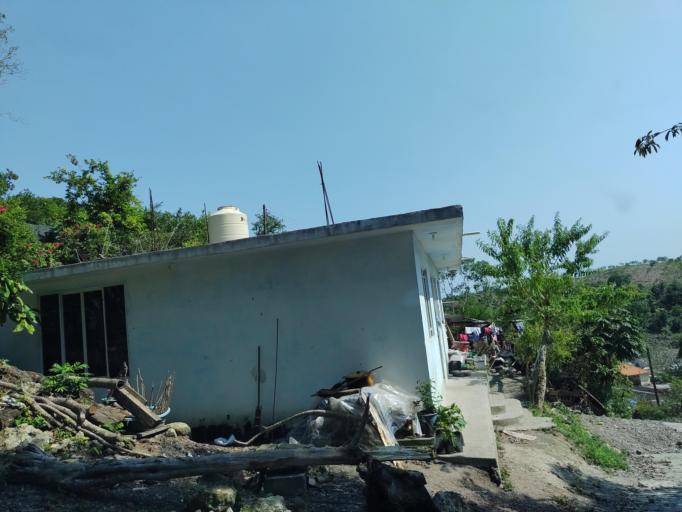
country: MX
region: Veracruz
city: Agua Dulce
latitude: 20.3376
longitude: -97.2045
